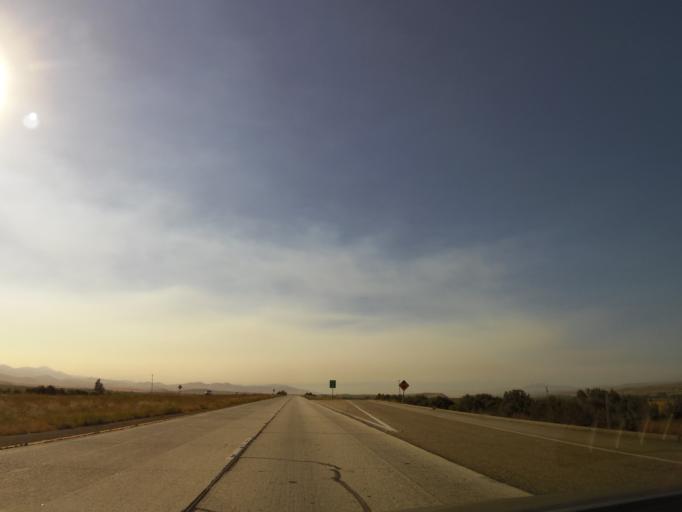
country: US
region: California
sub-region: Monterey County
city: King City
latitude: 36.0919
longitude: -121.0186
